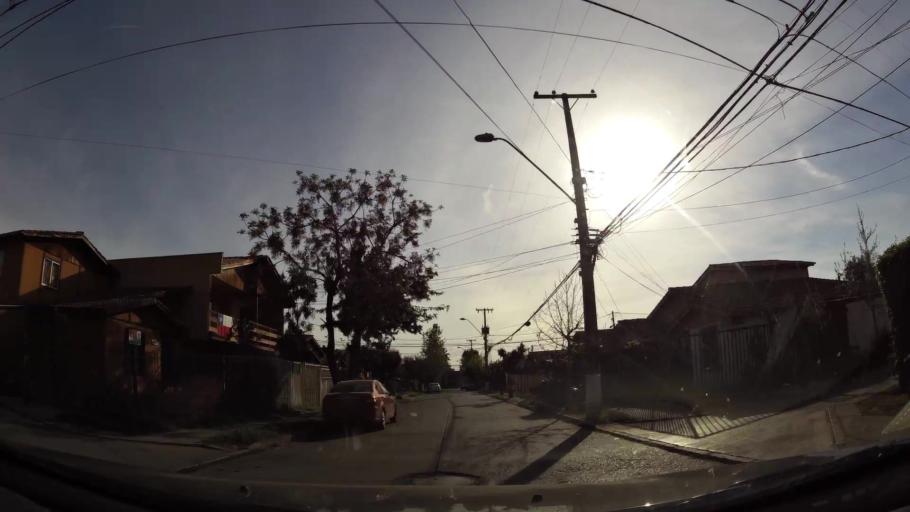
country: CL
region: Santiago Metropolitan
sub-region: Provincia de Cordillera
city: Puente Alto
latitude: -33.5784
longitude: -70.5681
